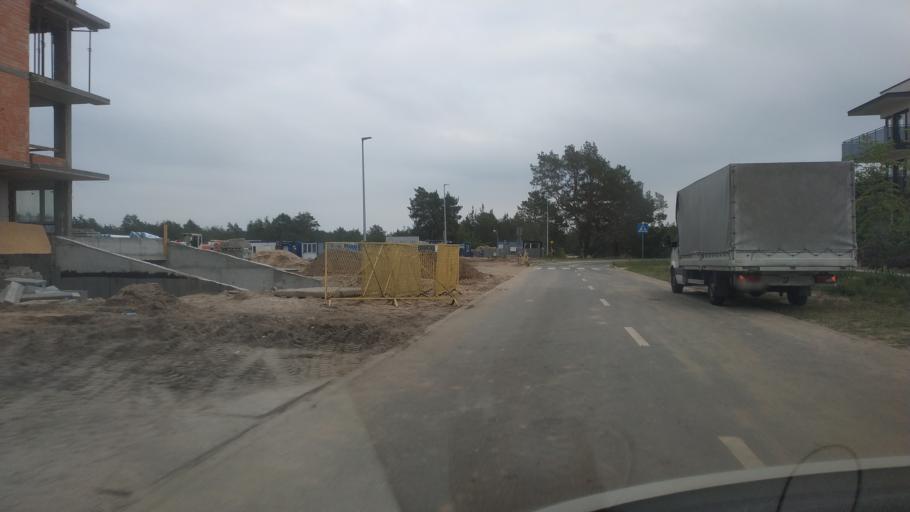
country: PL
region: Kujawsko-Pomorskie
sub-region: Torun
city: Torun
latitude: 53.0462
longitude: 18.6054
